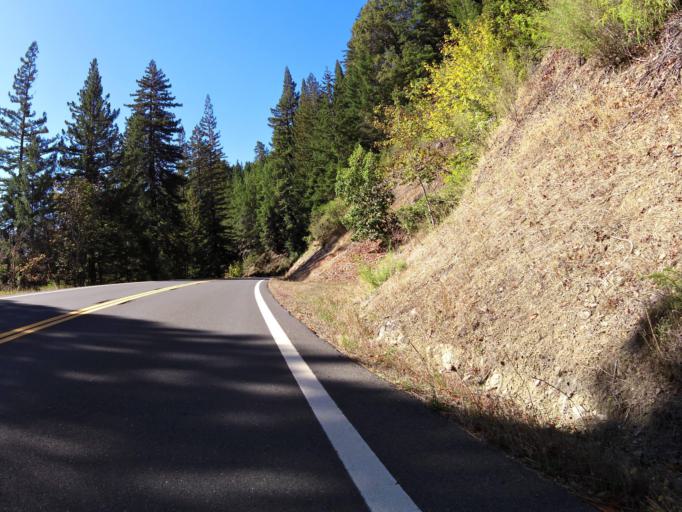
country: US
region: California
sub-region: Humboldt County
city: Redway
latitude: 39.8578
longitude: -123.7293
